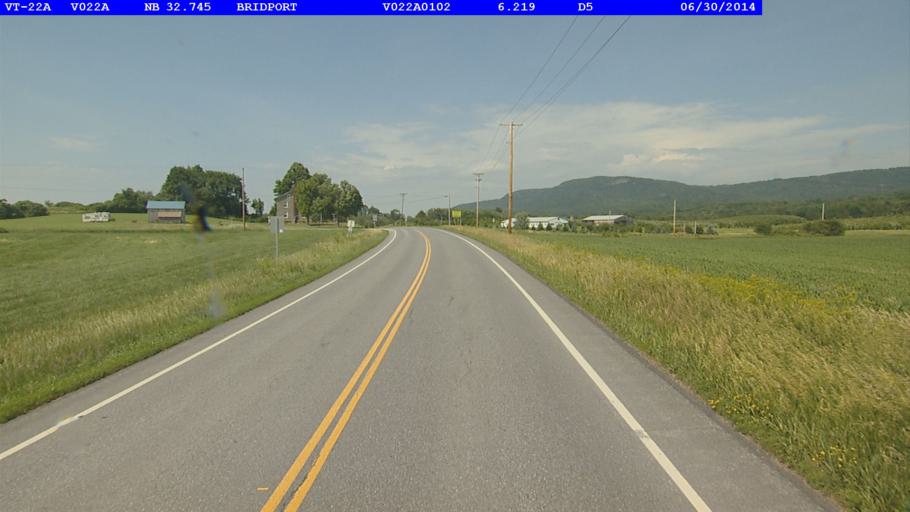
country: US
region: Vermont
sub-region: Addison County
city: Middlebury (village)
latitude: 44.0288
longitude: -73.3080
